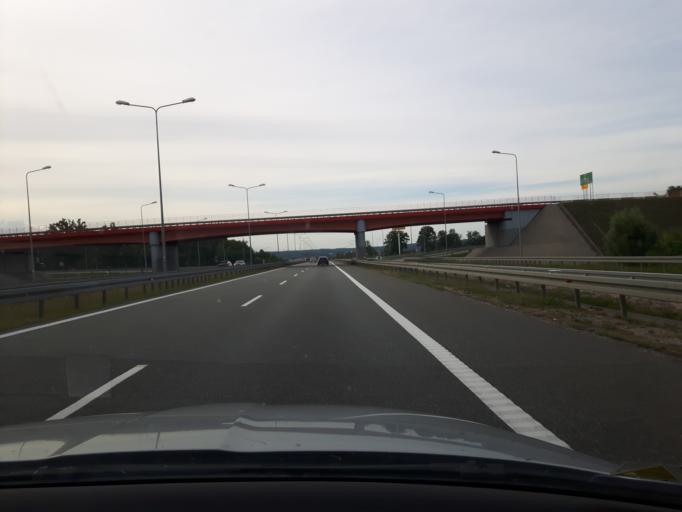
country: PL
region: Warmian-Masurian Voivodeship
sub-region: Powiat elblaski
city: Paslek
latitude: 54.0791
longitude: 19.6094
